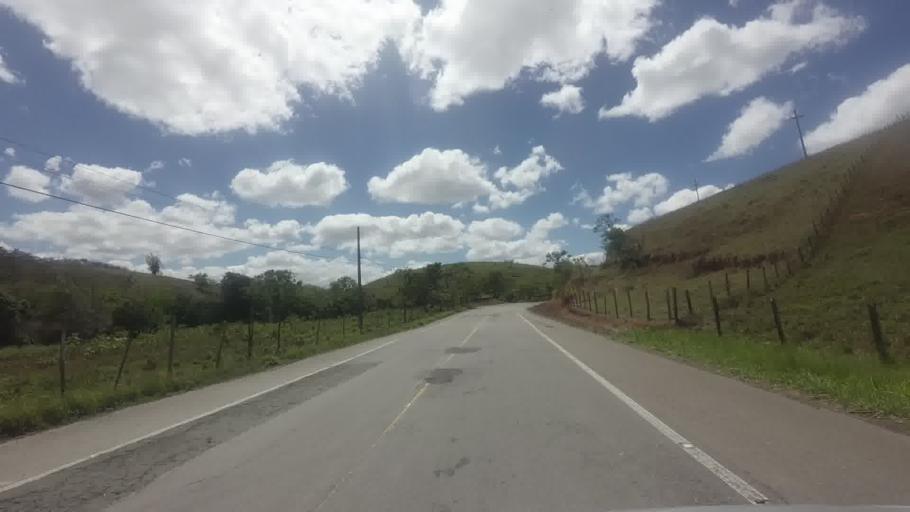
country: BR
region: Rio de Janeiro
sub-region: Santo Antonio De Padua
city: Santo Antonio de Padua
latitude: -21.6496
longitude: -42.2927
